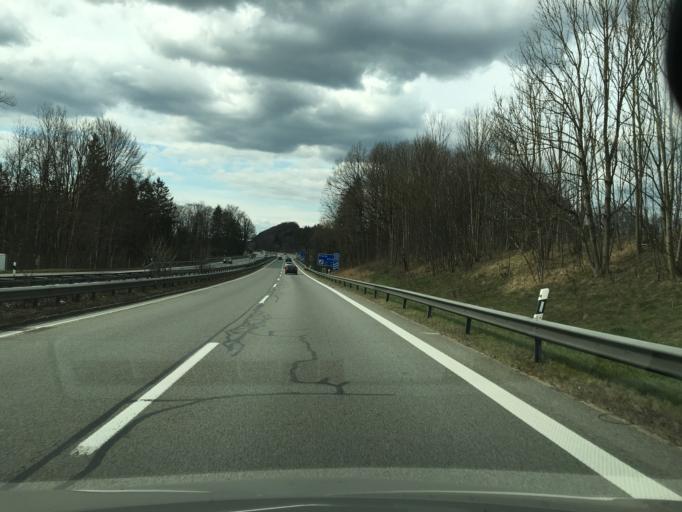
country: DE
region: Bavaria
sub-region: Upper Bavaria
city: Frasdorf
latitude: 47.8035
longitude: 12.3021
